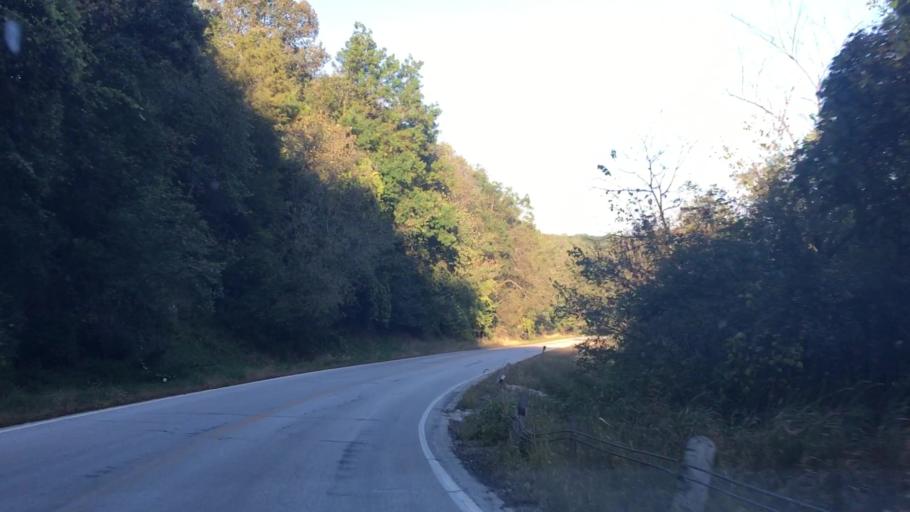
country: US
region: Minnesota
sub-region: Fillmore County
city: Chatfield
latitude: 43.8178
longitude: -92.0552
